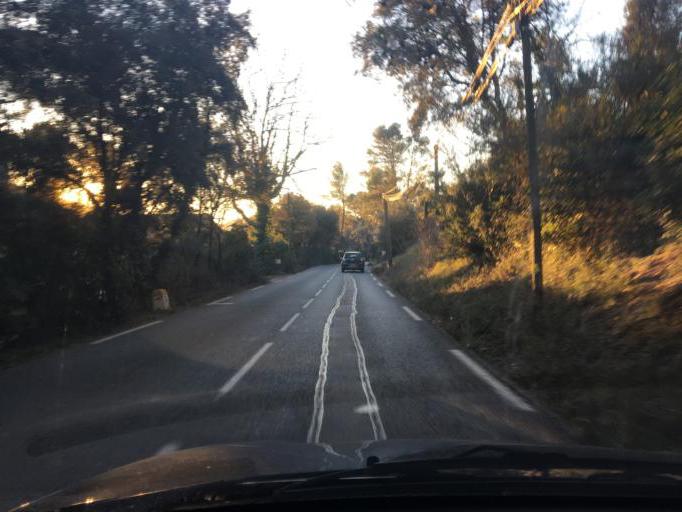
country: FR
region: Provence-Alpes-Cote d'Azur
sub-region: Departement du Var
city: Taradeau
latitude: 43.4560
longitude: 6.4214
